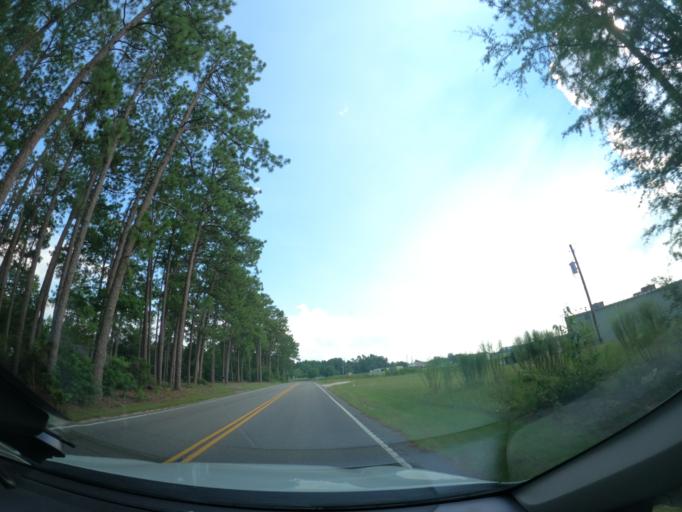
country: US
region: South Carolina
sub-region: Barnwell County
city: Williston
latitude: 33.4858
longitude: -81.5166
